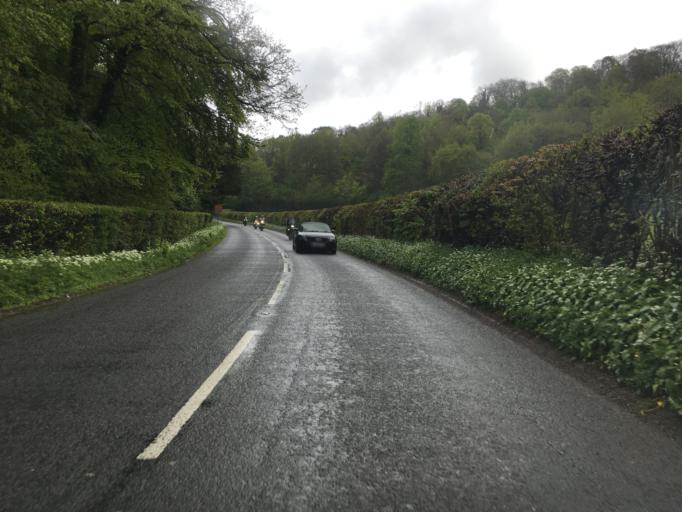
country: GB
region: England
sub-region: North Somerset
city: Blagdon
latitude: 51.3277
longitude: -2.7320
